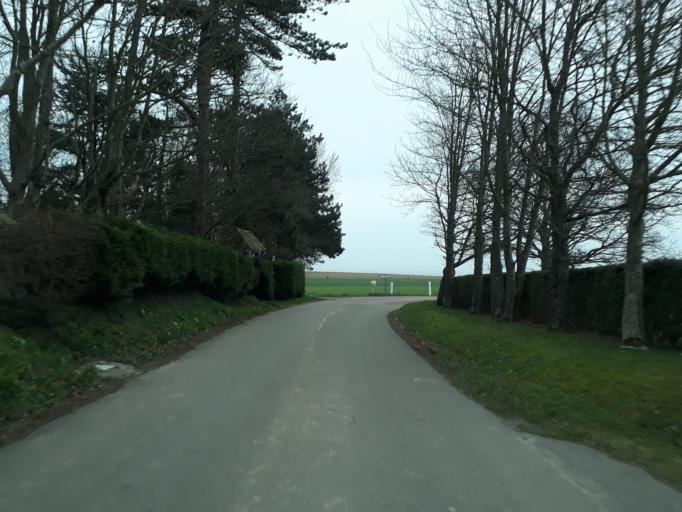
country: FR
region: Haute-Normandie
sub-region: Departement de la Seine-Maritime
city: Les Loges
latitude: 49.7288
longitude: 0.2822
